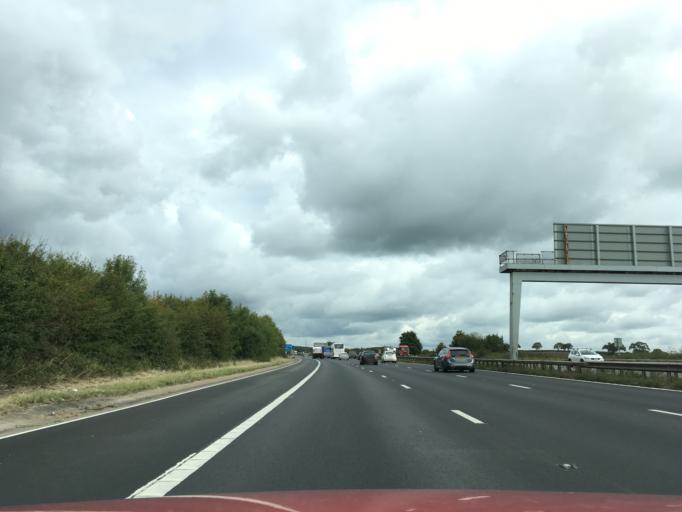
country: GB
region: England
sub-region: South Gloucestershire
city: Alveston
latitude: 51.5588
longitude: -2.5361
